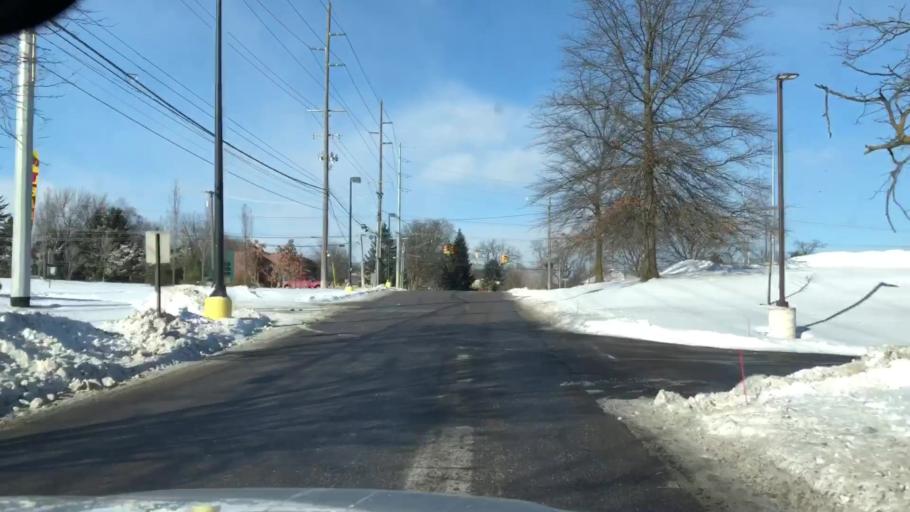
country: US
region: Michigan
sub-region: Wayne County
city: Northville
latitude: 42.4377
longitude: -83.4388
